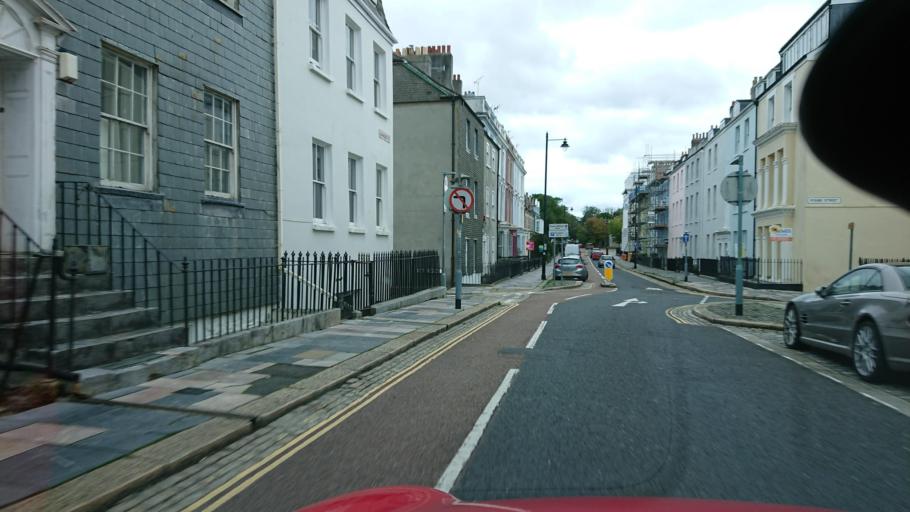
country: GB
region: England
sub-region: Plymouth
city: Plymouth
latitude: 50.3649
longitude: -4.1616
